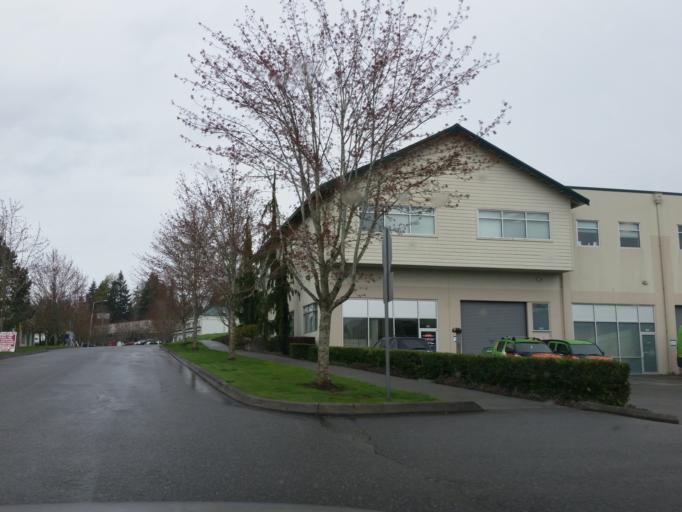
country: US
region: Washington
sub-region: Snohomish County
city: Fobes Hill
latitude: 47.9341
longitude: -122.1056
